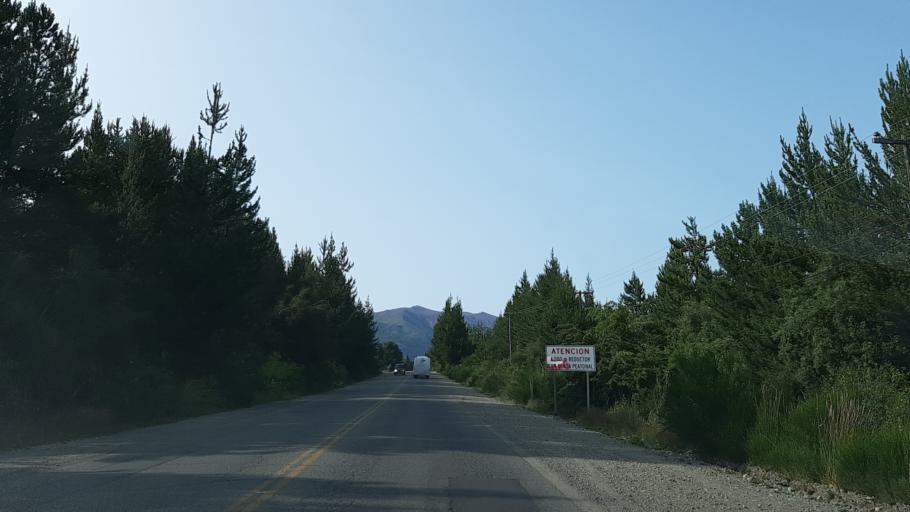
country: AR
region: Rio Negro
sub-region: Departamento de Bariloche
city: San Carlos de Bariloche
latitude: -41.1463
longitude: -71.4099
